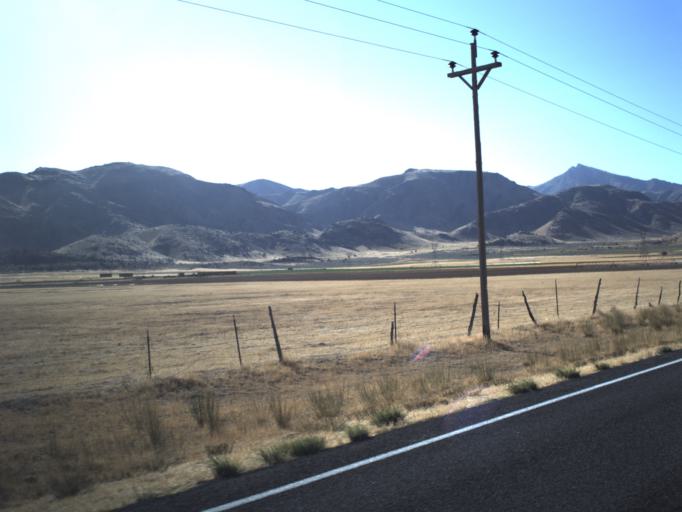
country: US
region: Utah
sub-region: Millard County
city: Delta
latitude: 39.5056
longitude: -112.2691
